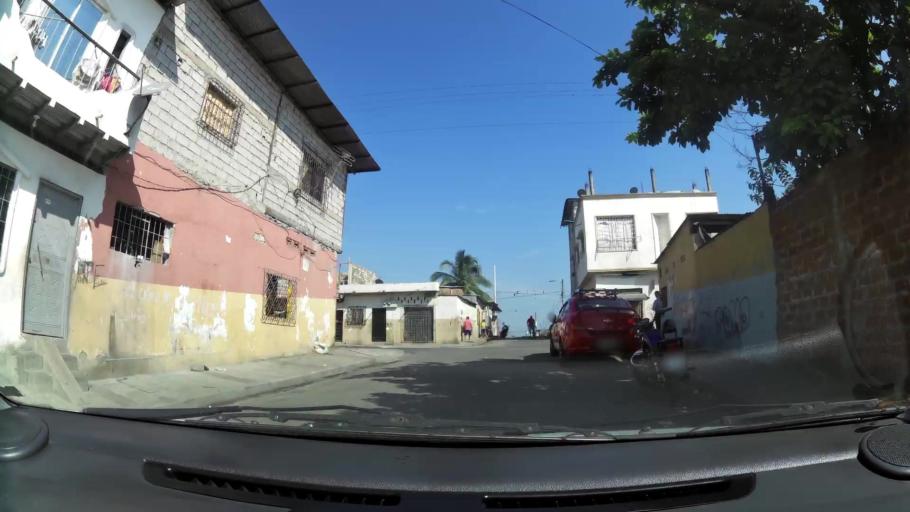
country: EC
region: Guayas
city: Eloy Alfaro
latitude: -2.0996
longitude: -79.9244
